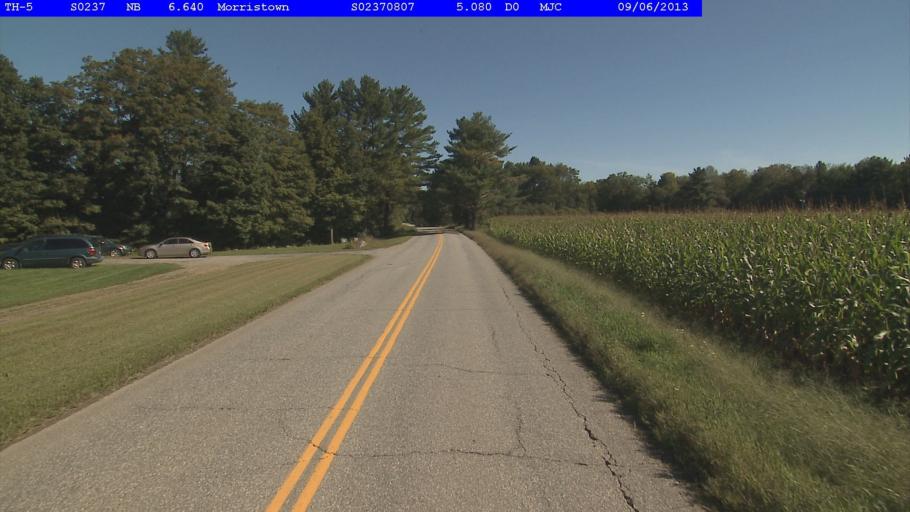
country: US
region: Vermont
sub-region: Lamoille County
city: Morristown
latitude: 44.5681
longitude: -72.6187
